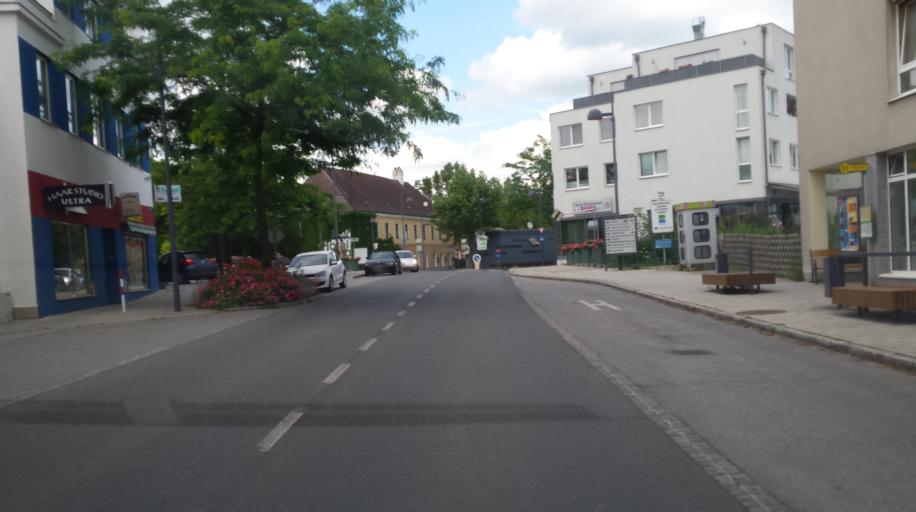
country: AT
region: Lower Austria
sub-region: Politischer Bezirk Mistelbach
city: Wolkersdorf im Weinviertel
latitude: 48.3840
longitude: 16.5145
